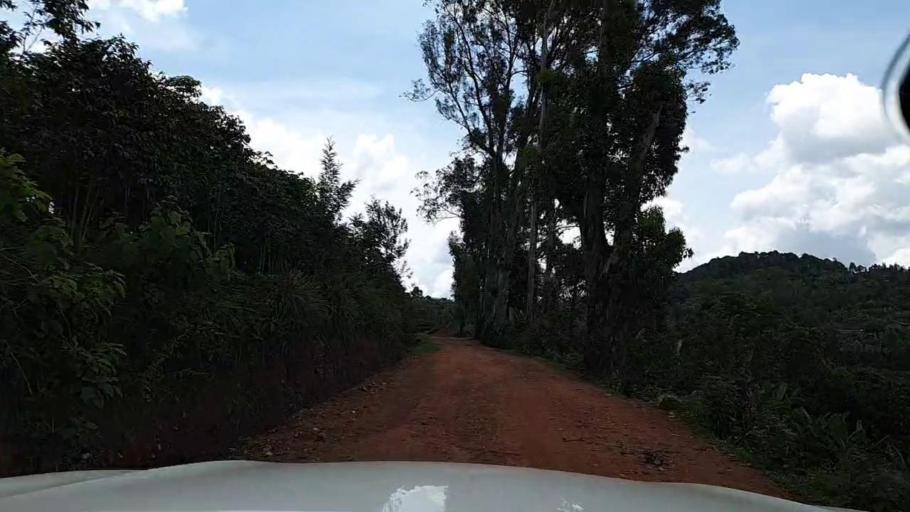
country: RW
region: Southern Province
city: Butare
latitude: -2.7522
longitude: 29.7578
